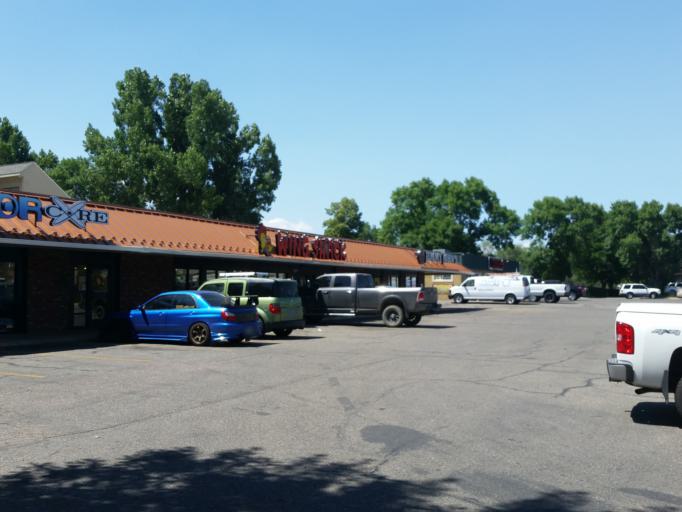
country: US
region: Colorado
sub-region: Larimer County
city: Fort Collins
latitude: 40.5734
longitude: -105.0581
